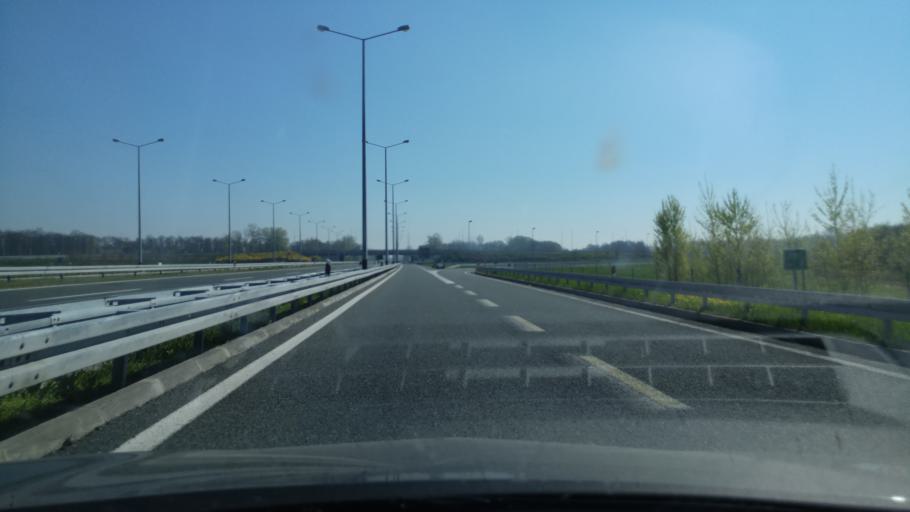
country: HR
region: Brodsko-Posavska
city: Vrpolje
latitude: 45.1448
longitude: 18.3058
